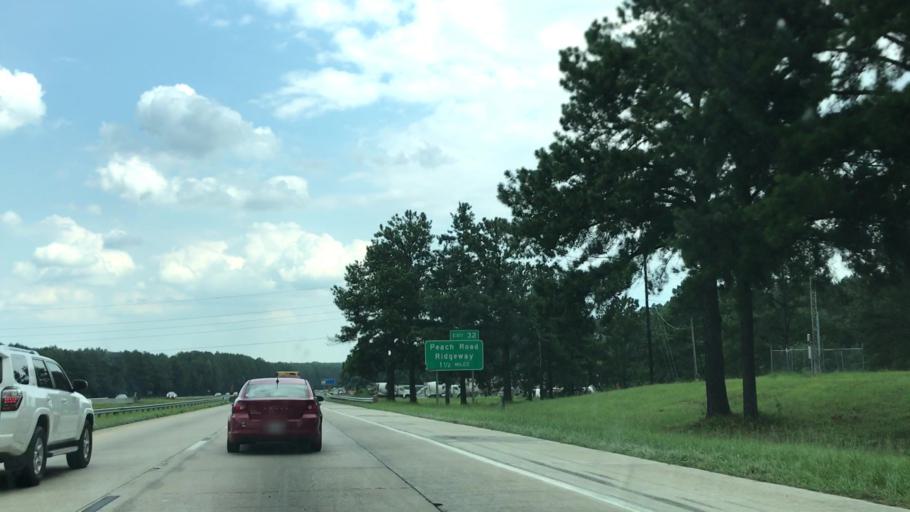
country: US
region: South Carolina
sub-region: Richland County
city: Blythewood
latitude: 34.3091
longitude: -81.0009
